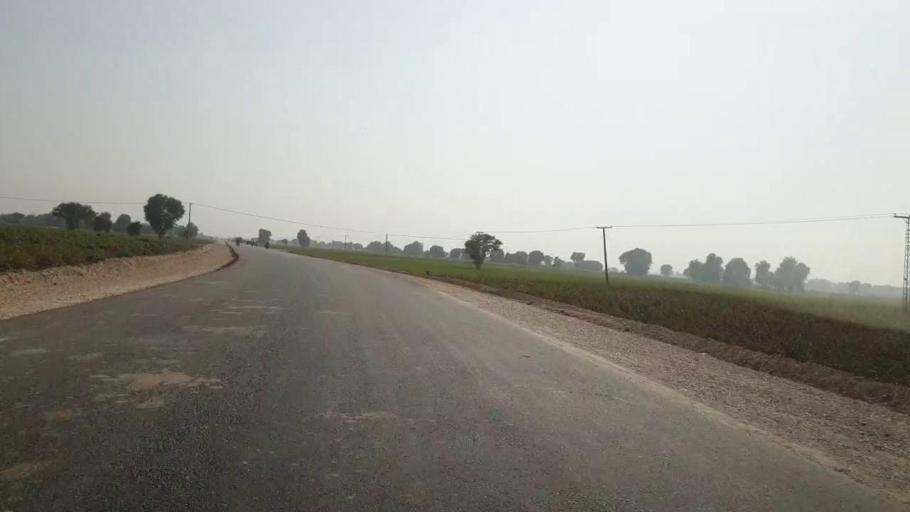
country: PK
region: Sindh
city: Dadu
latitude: 26.6739
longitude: 67.7765
